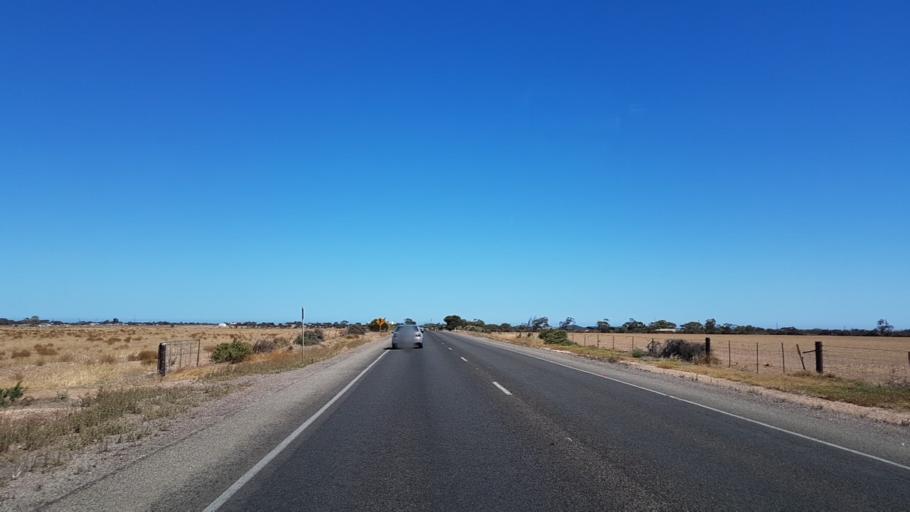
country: AU
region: South Australia
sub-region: Copper Coast
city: Wallaroo
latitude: -33.9465
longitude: 137.6662
